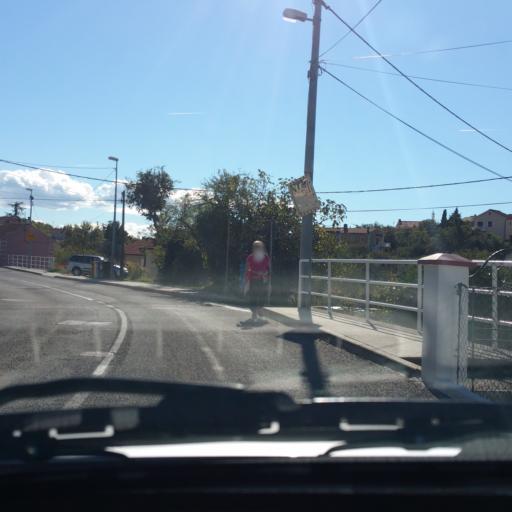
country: HR
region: Primorsko-Goranska
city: Omisalj
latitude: 45.2132
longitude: 14.5571
